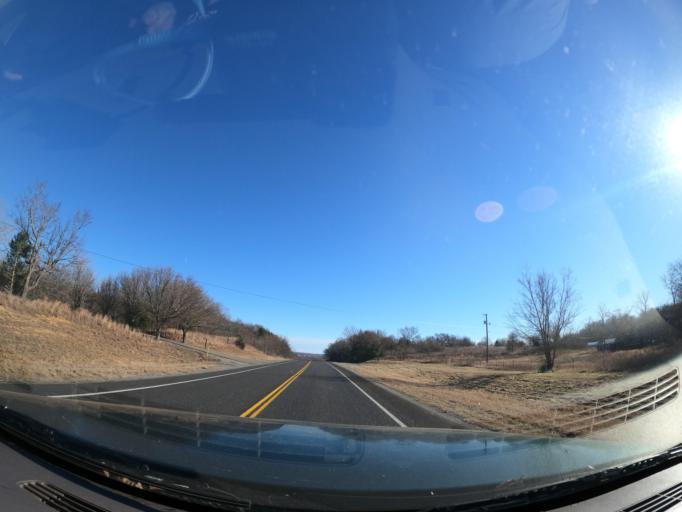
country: US
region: Oklahoma
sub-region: McIntosh County
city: Eufaula
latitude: 35.2528
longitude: -95.5740
